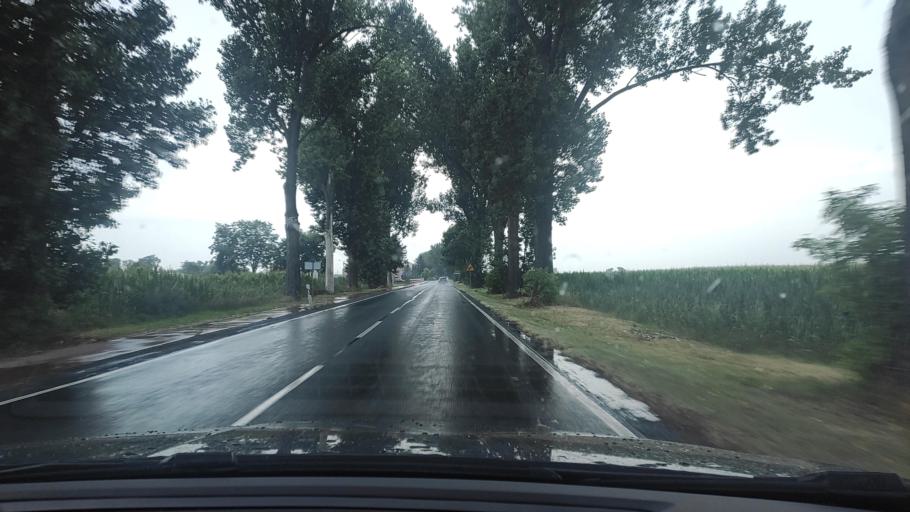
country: PL
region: Greater Poland Voivodeship
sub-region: Powiat sredzki
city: Sroda Wielkopolska
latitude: 52.2456
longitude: 17.2495
